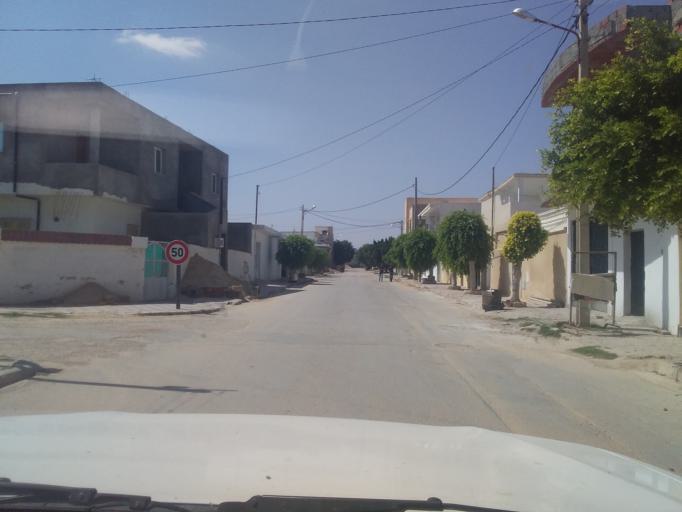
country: TN
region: Qabis
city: Matmata
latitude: 33.6143
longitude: 10.2884
